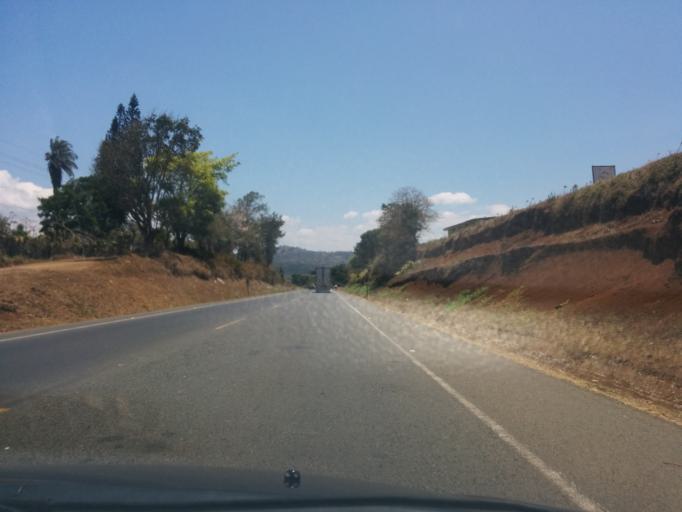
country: CR
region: Alajuela
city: San Rafael
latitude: 10.0761
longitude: -84.4761
